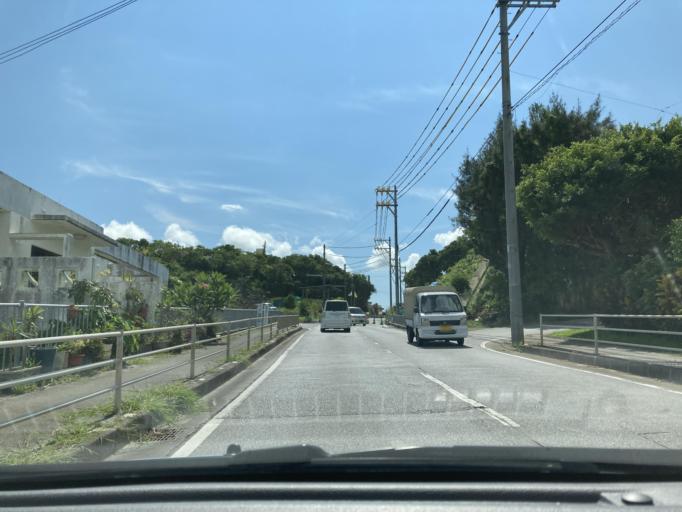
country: JP
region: Okinawa
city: Tomigusuku
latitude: 26.1796
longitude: 127.7432
